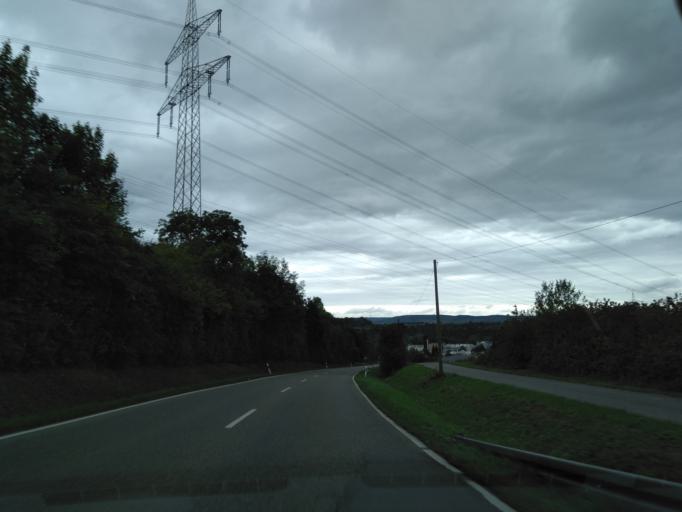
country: DE
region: Baden-Wuerttemberg
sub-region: Regierungsbezirk Stuttgart
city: Markgroningen
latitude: 48.9296
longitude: 9.0643
